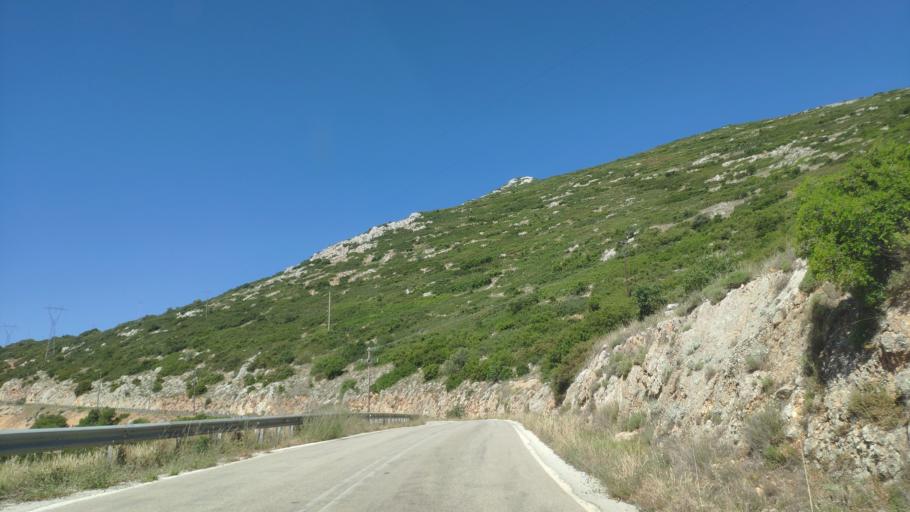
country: GR
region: Peloponnese
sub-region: Nomos Korinthias
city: Khiliomodhi
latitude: 37.7625
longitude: 22.8814
